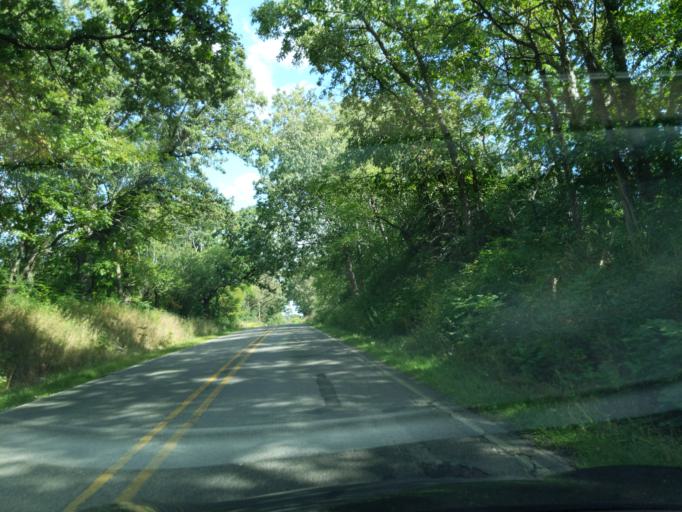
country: US
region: Michigan
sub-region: Jackson County
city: Jackson
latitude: 42.2957
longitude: -84.4892
